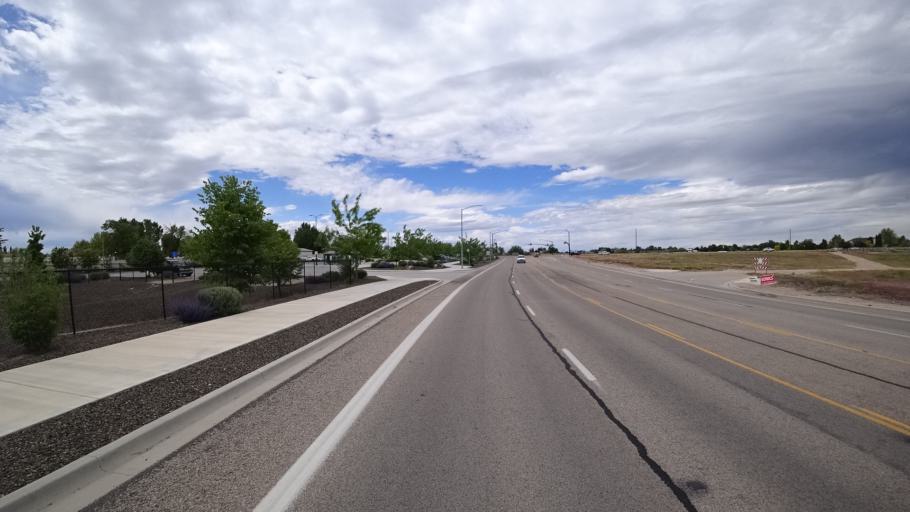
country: US
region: Idaho
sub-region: Ada County
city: Meridian
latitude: 43.5849
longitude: -116.4317
